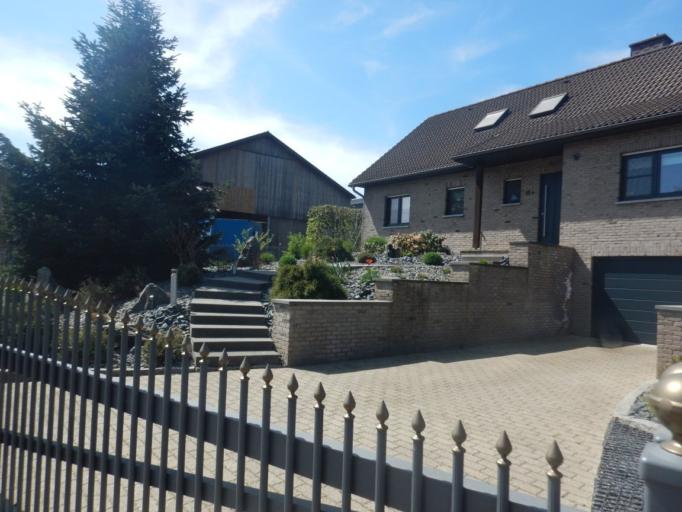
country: LU
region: Diekirch
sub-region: Canton de Redange
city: Redange-sur-Attert
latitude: 49.7566
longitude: 5.9139
